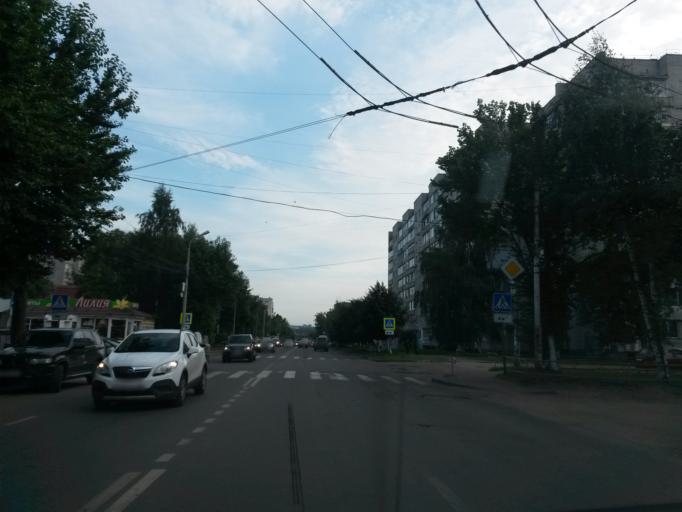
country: RU
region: Jaroslavl
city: Yaroslavl
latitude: 57.6253
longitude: 39.8486
